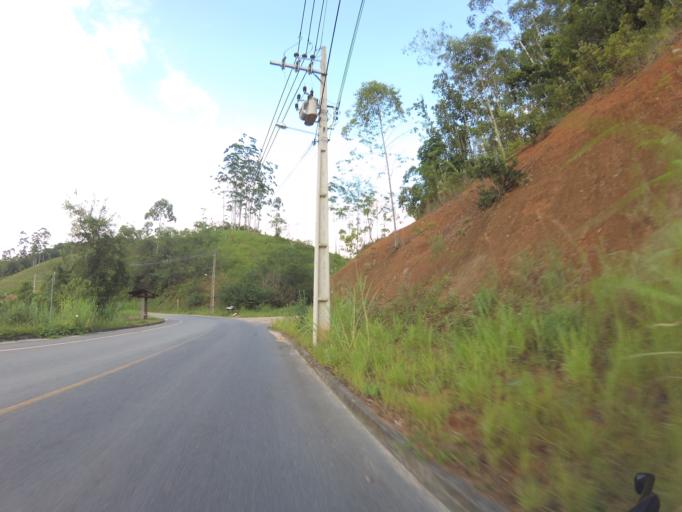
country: BR
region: Santa Catarina
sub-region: Pomerode
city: Pomerode
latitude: -26.8073
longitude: -49.1604
